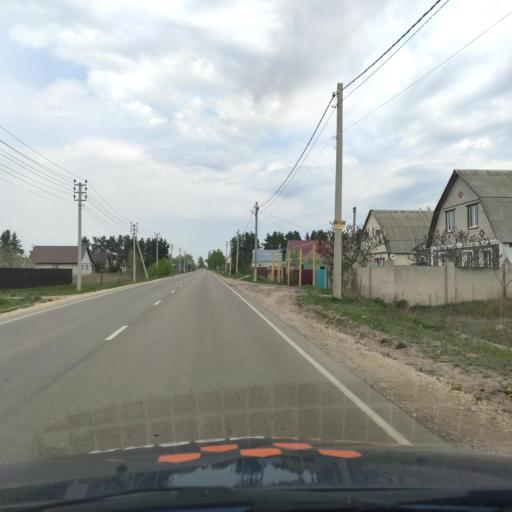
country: RU
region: Voronezj
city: Podgornoye
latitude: 51.8739
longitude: 39.1731
